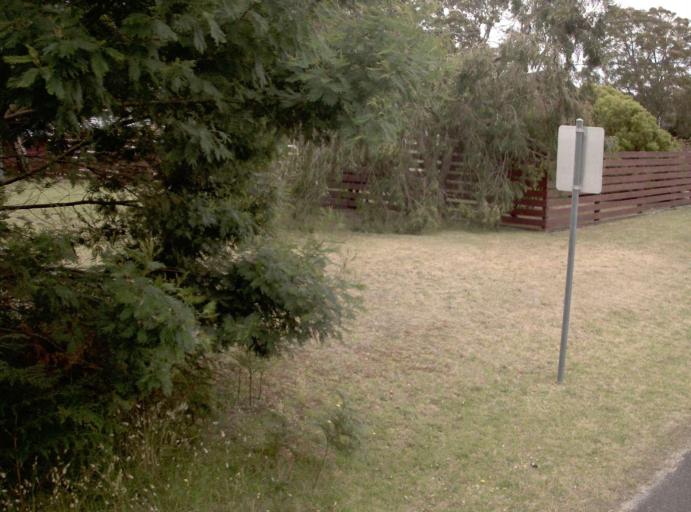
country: AU
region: Victoria
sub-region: East Gippsland
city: Bairnsdale
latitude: -38.0545
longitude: 147.5732
